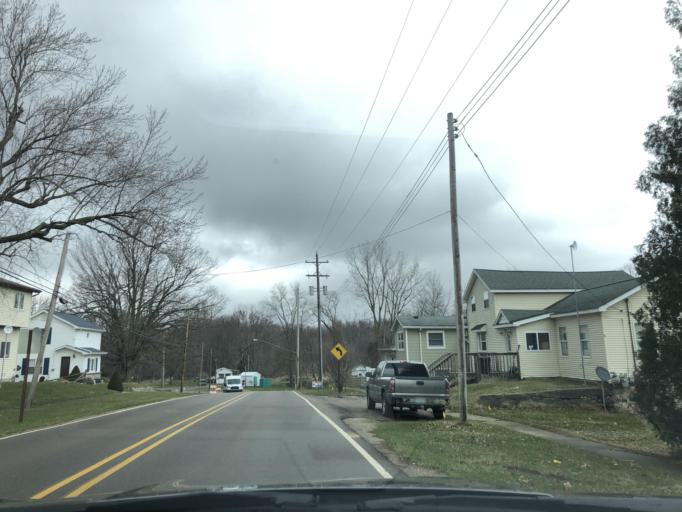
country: US
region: Michigan
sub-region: Clinton County
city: Fowler
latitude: 43.1057
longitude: -84.6922
